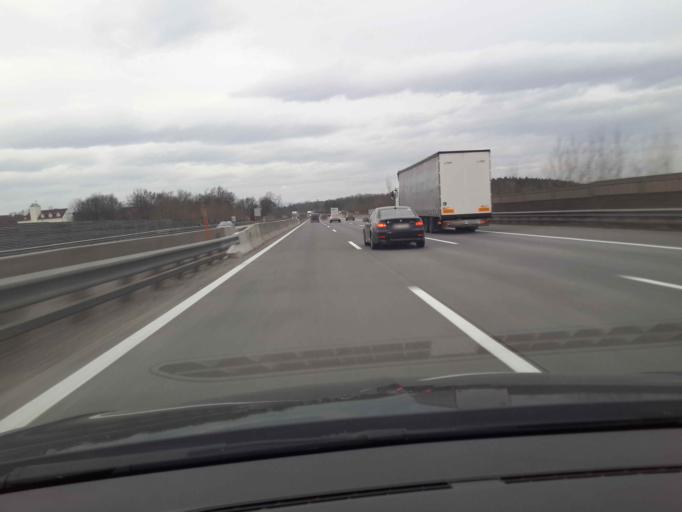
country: AT
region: Lower Austria
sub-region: Politischer Bezirk Amstetten
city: Zeillern
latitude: 48.1306
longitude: 14.8279
